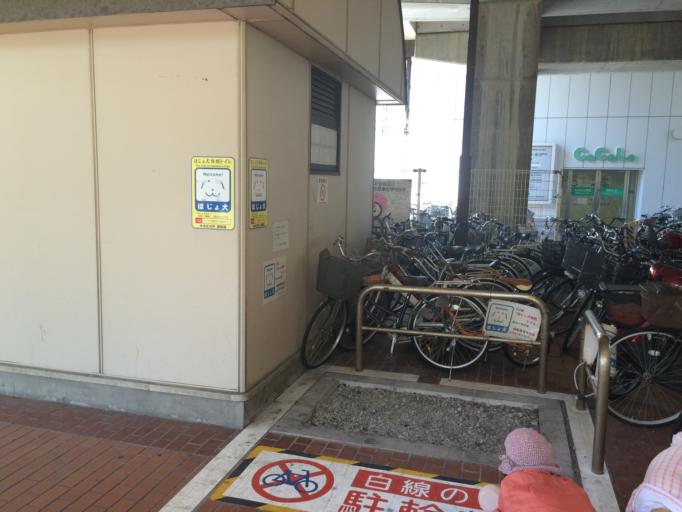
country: JP
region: Niigata
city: Niigata-shi
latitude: 37.9111
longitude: 139.0631
